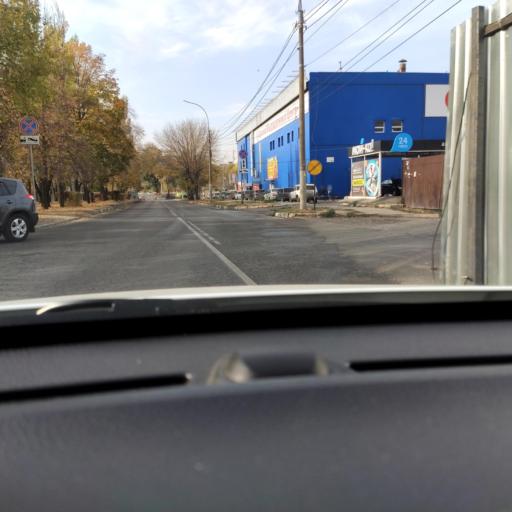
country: RU
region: Voronezj
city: Voronezh
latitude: 51.6673
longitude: 39.1742
